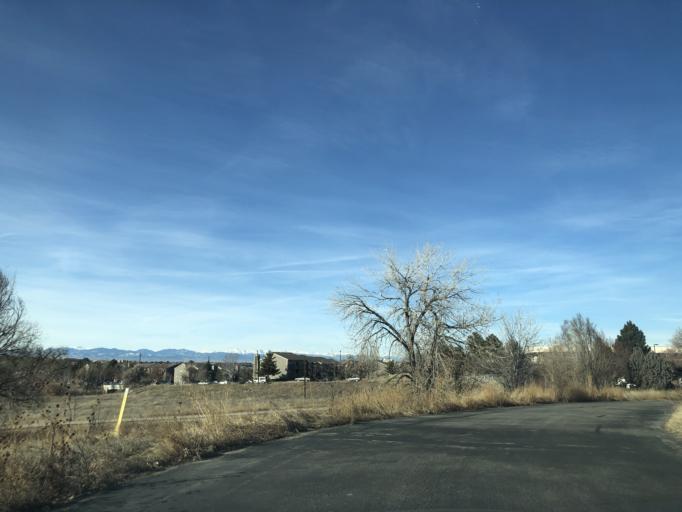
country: US
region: Colorado
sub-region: Adams County
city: Aurora
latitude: 39.7177
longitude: -104.8043
